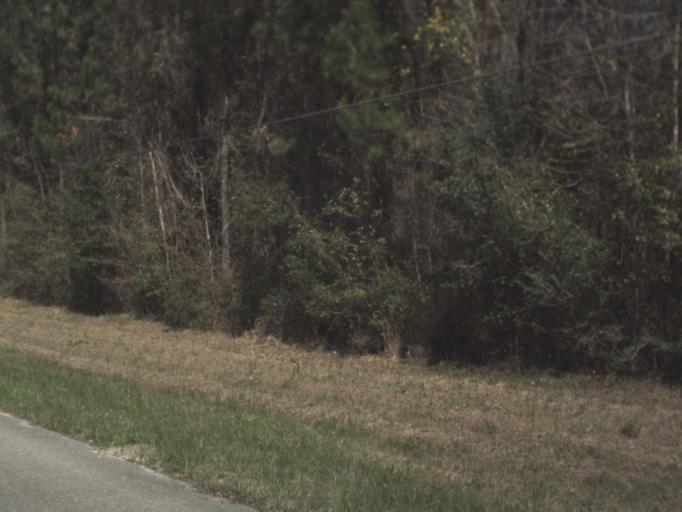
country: US
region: Florida
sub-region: Leon County
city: Woodville
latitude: 30.2255
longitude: -84.2275
